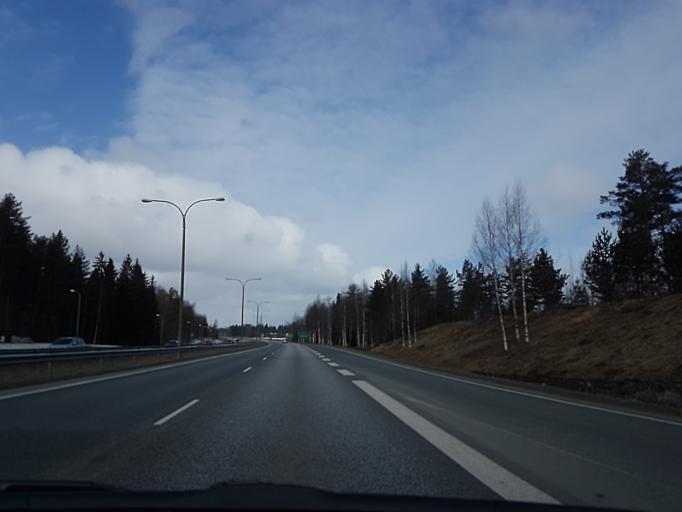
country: FI
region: North Karelia
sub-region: Joensuu
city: Joensuu
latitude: 62.6187
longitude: 29.7283
